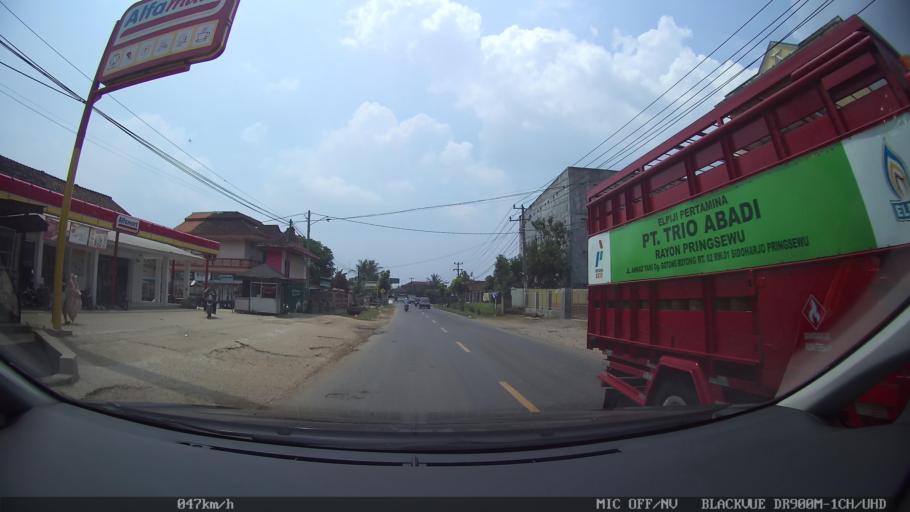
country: ID
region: Lampung
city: Pringsewu
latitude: -5.3766
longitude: 105.0141
